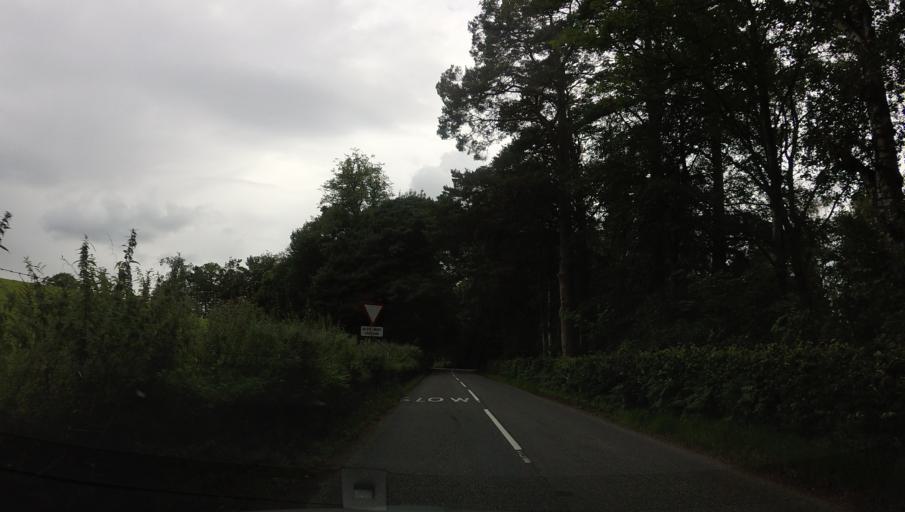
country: GB
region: Scotland
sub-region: Aberdeenshire
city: Aboyne
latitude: 57.0594
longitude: -2.7049
